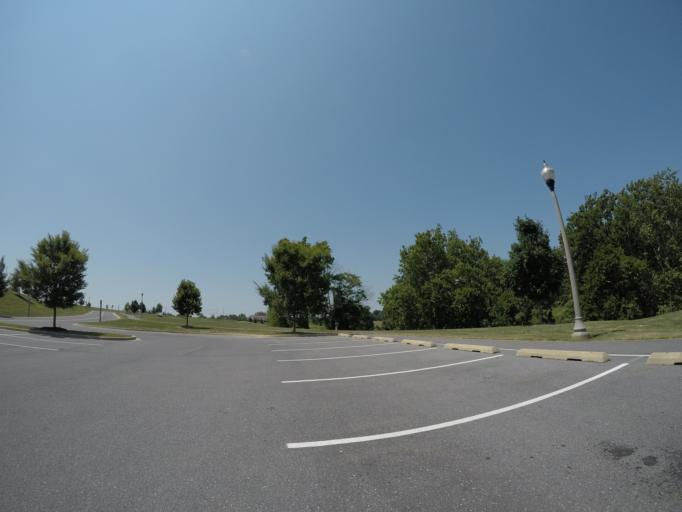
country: US
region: Maryland
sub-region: Frederick County
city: Urbana
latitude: 39.3394
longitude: -77.3663
